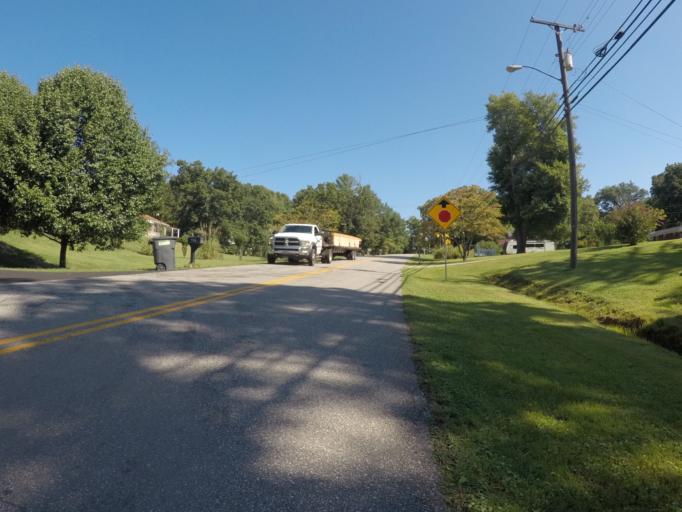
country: US
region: Kentucky
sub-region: Greenup County
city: Russell
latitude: 38.5182
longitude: -82.6958
